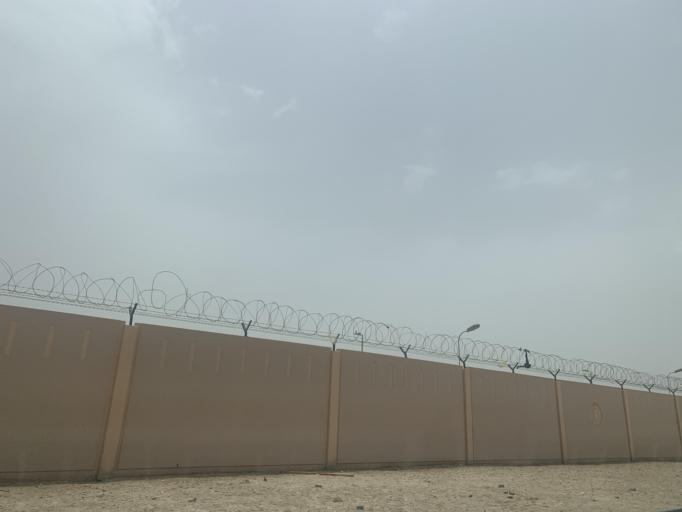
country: BH
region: Northern
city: Sitrah
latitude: 26.1767
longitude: 50.6300
